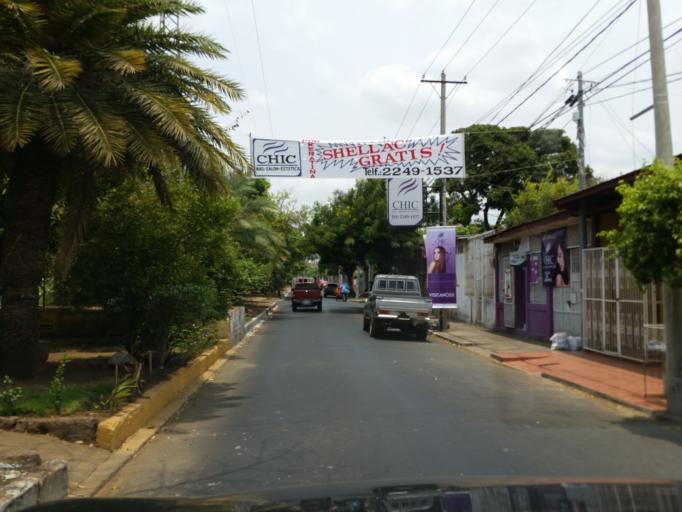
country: NI
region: Managua
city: Managua
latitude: 12.1421
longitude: -86.2336
